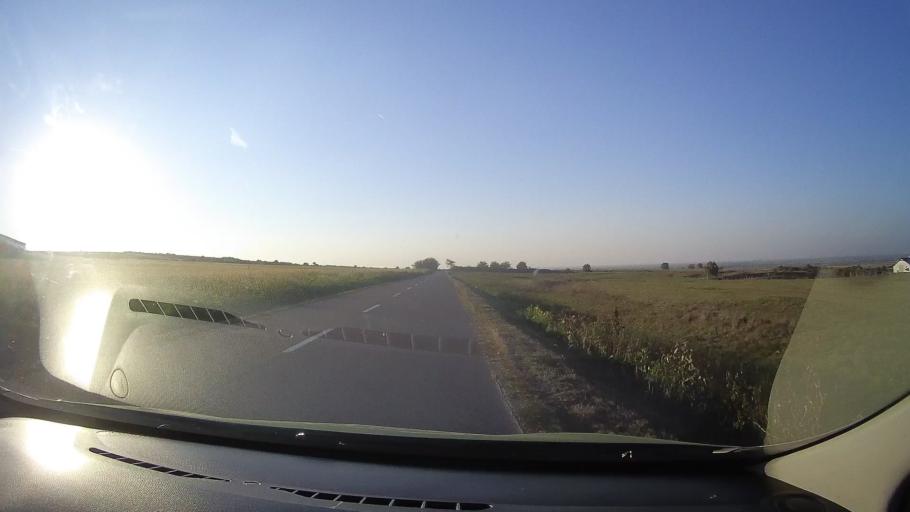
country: RO
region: Bihor
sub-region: Comuna Cetariu
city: Cetariu
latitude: 47.1524
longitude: 21.9922
